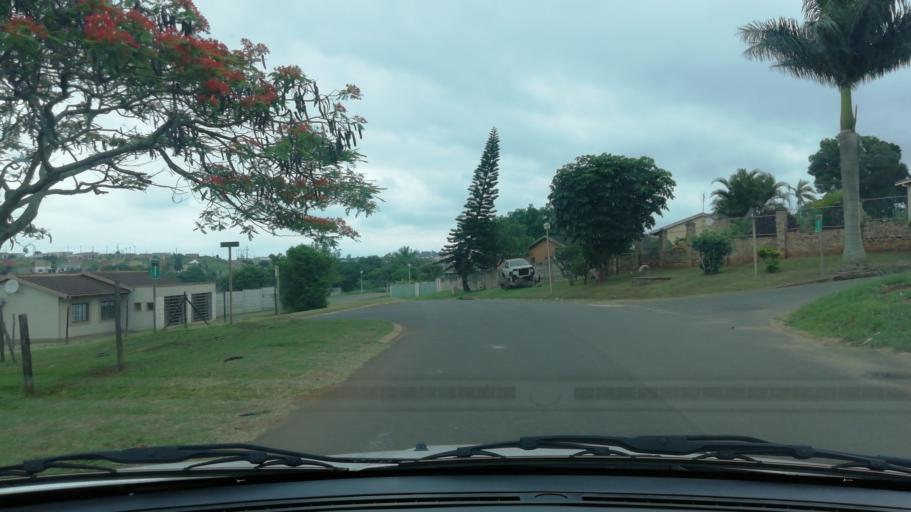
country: ZA
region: KwaZulu-Natal
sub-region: uThungulu District Municipality
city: Empangeni
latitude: -28.7618
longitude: 31.8836
